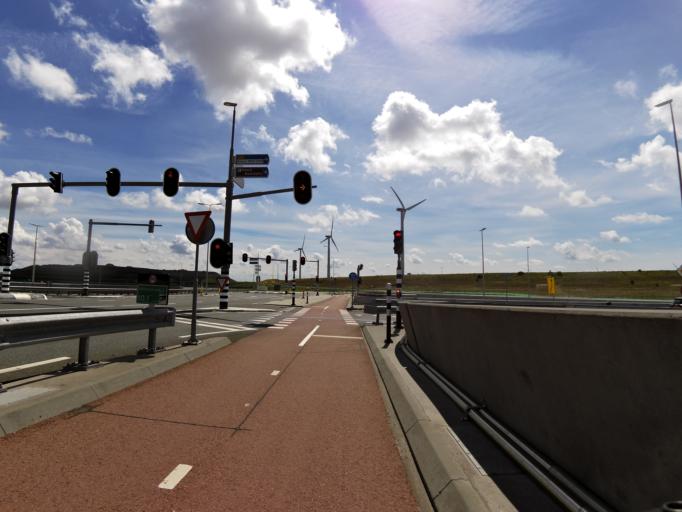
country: NL
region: South Holland
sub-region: Gemeente Goeree-Overflakkee
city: Goedereede
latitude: 51.9329
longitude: 4.0192
